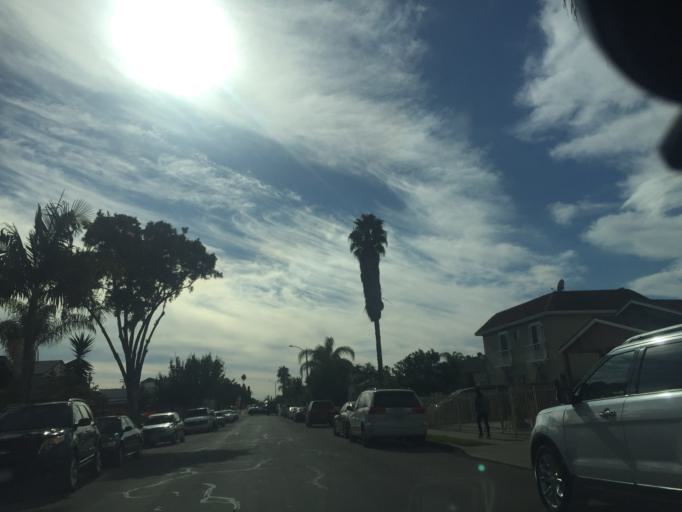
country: US
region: California
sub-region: San Diego County
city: Lemon Grove
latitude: 32.7508
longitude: -117.0944
